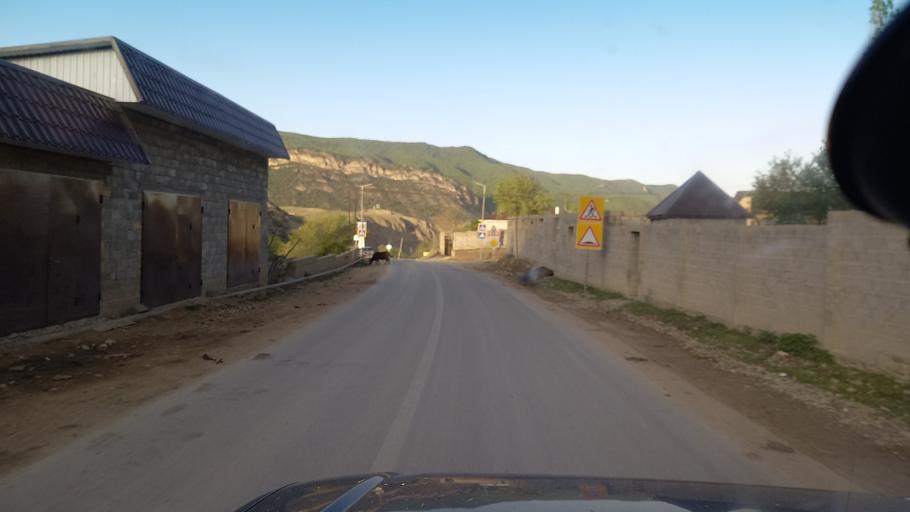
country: RU
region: Dagestan
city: Khuchni
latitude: 41.9747
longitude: 47.8938
